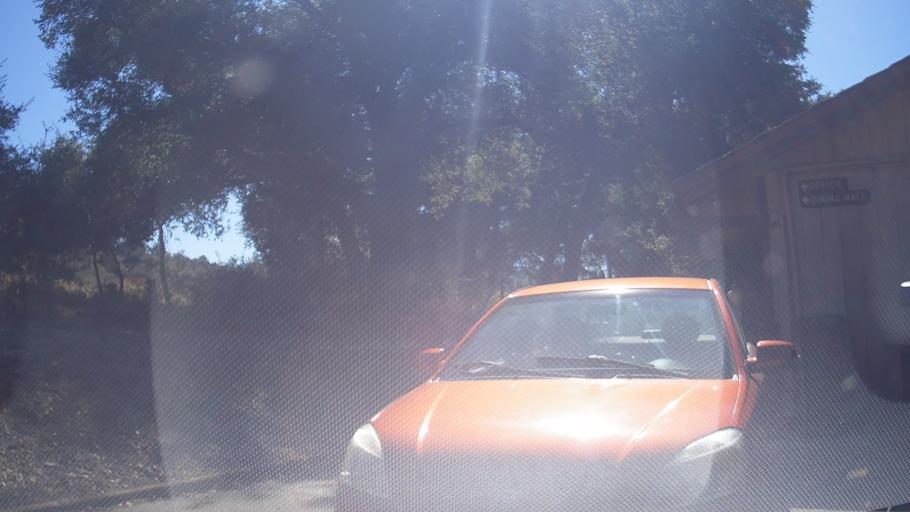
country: US
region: California
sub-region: San Diego County
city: Julian
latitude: 33.0394
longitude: -116.6401
